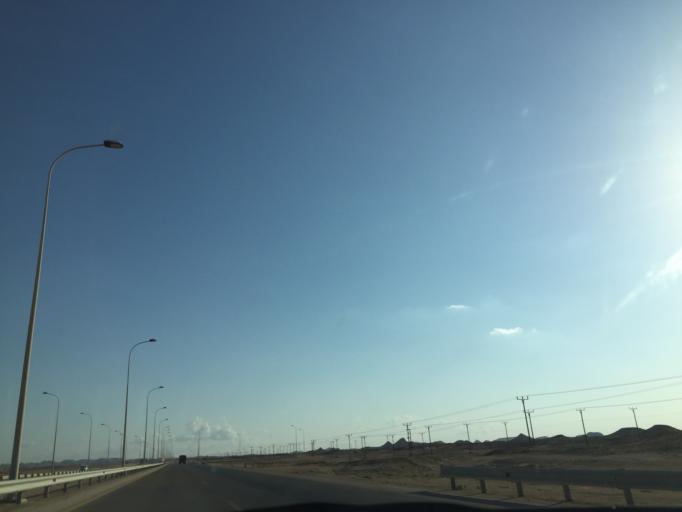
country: OM
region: Zufar
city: Salalah
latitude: 17.5340
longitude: 54.0555
